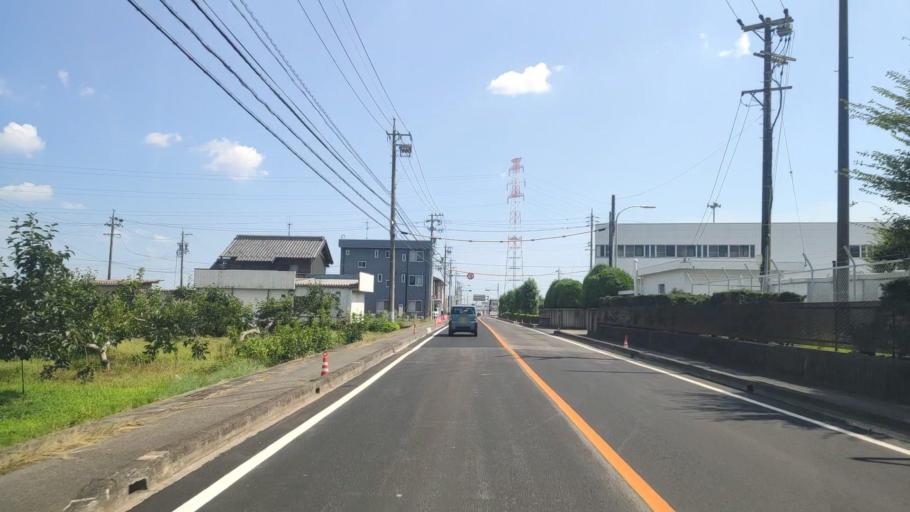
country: JP
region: Gifu
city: Godo
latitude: 35.4643
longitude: 136.6757
